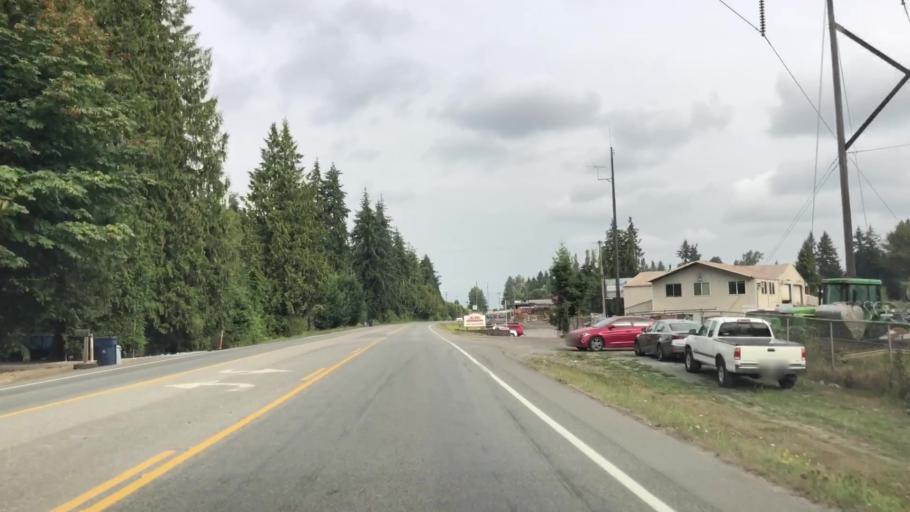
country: US
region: Washington
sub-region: Snohomish County
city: Fobes Hill
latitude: 47.9512
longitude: -122.1163
